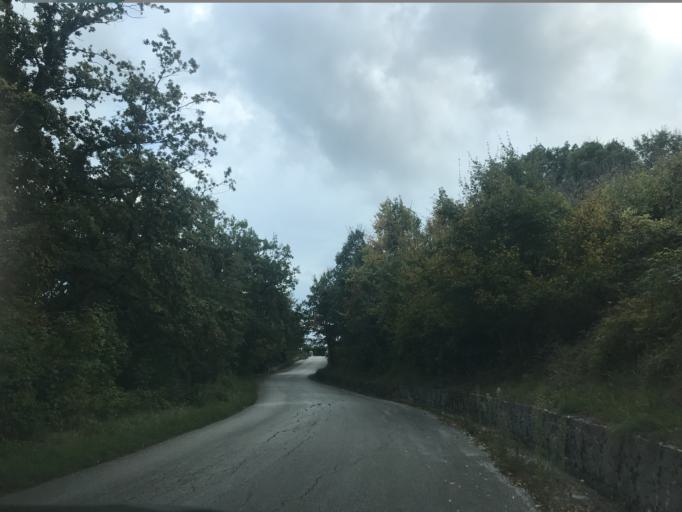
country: IT
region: Molise
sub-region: Provincia di Campobasso
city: Duronia
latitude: 41.6613
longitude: 14.4612
